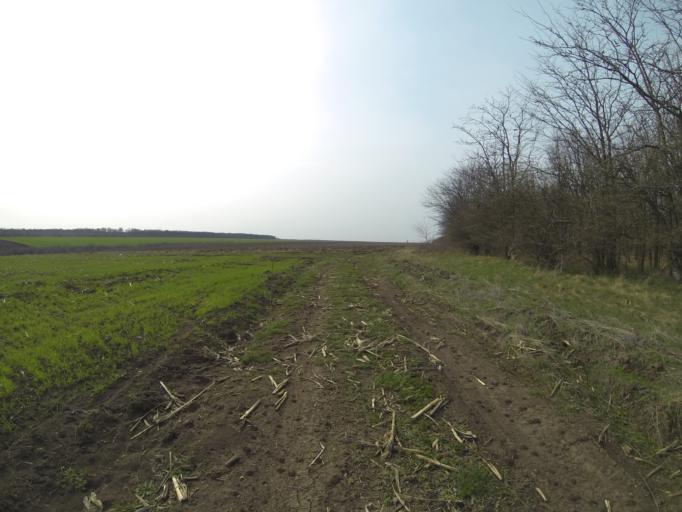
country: RO
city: Varvoru
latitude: 44.2715
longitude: 23.6629
